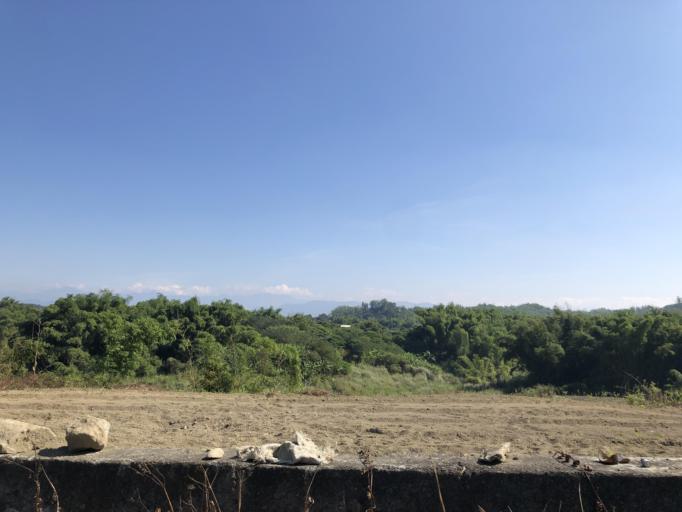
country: TW
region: Taiwan
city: Yujing
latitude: 23.0597
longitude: 120.3803
